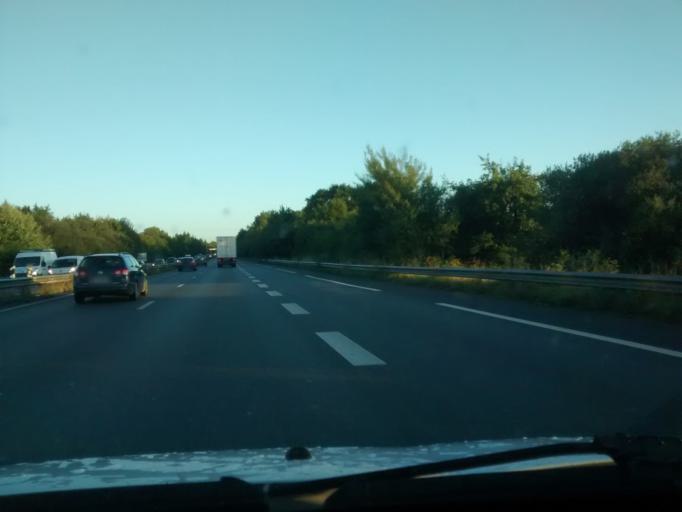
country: FR
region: Brittany
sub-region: Departement d'Ille-et-Vilaine
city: Montgermont
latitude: 48.1572
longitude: -1.7038
